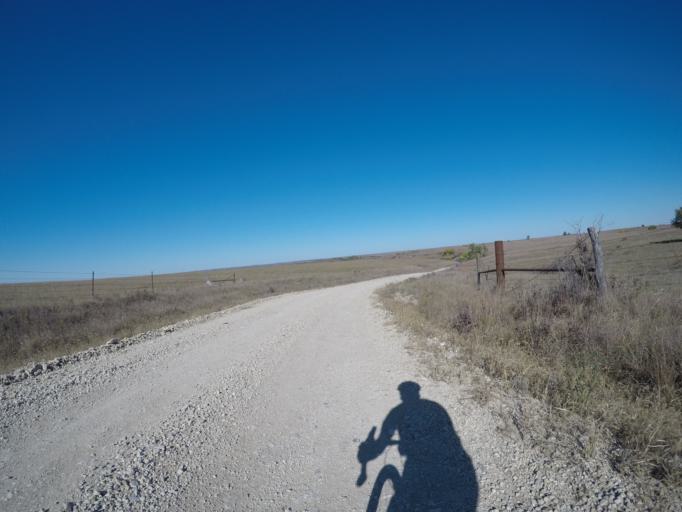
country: US
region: Kansas
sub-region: Wabaunsee County
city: Alma
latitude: 38.9208
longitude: -96.3902
